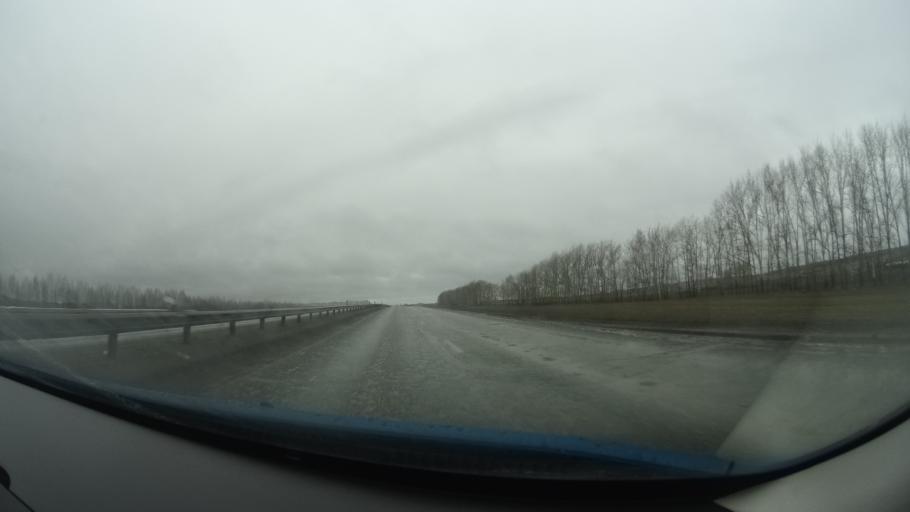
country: RU
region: Bashkortostan
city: Dmitriyevka
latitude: 54.6792
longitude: 55.3398
